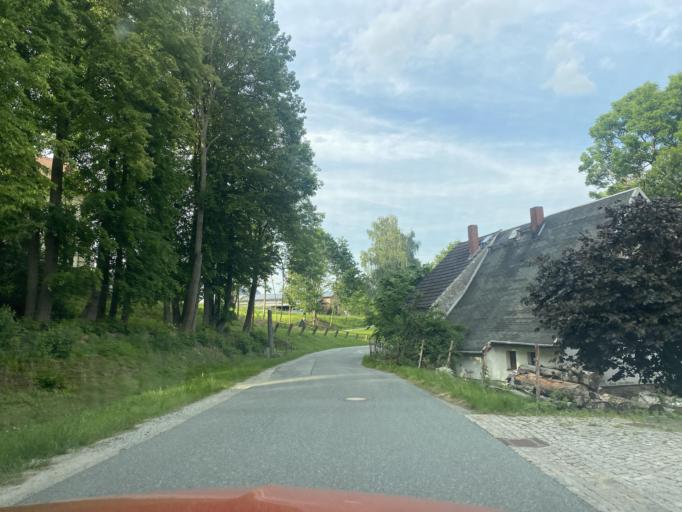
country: DE
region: Saxony
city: Grosshennersdorf
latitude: 51.0225
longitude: 14.7910
